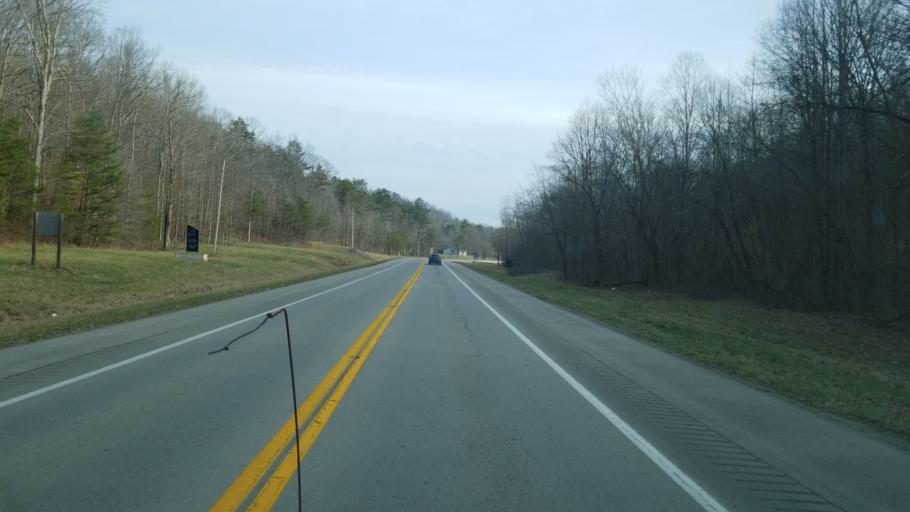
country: US
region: Kentucky
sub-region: Russell County
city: Russell Springs
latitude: 37.1583
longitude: -85.0208
